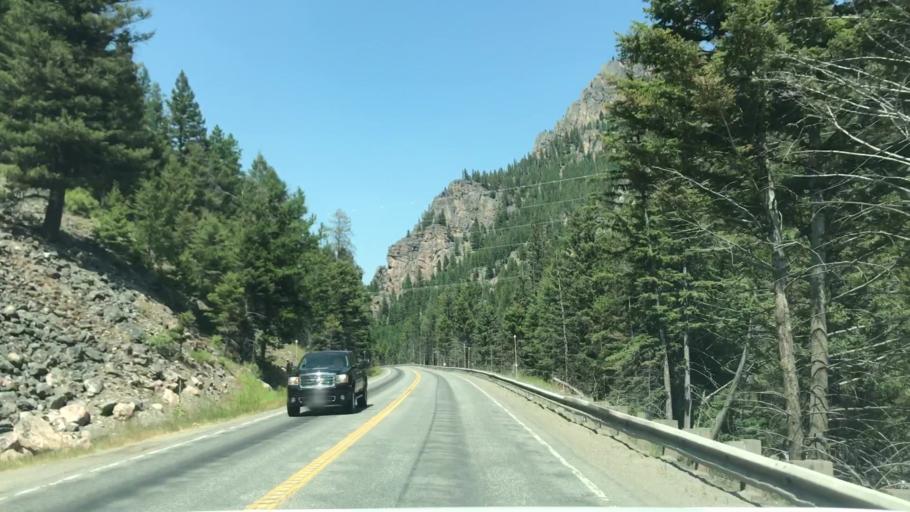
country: US
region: Montana
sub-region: Gallatin County
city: Big Sky
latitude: 45.4095
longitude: -111.2272
